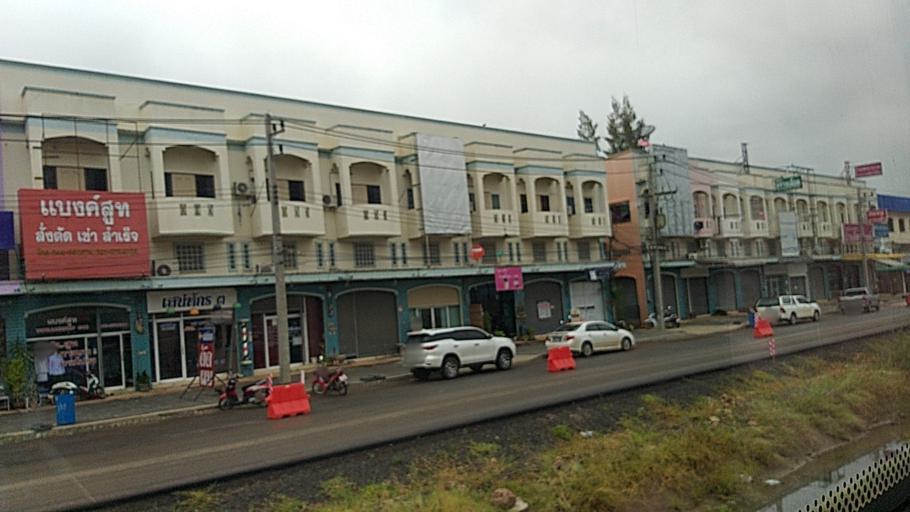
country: TH
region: Nakhon Ratchasima
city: Nakhon Ratchasima
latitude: 14.9951
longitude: 102.0791
